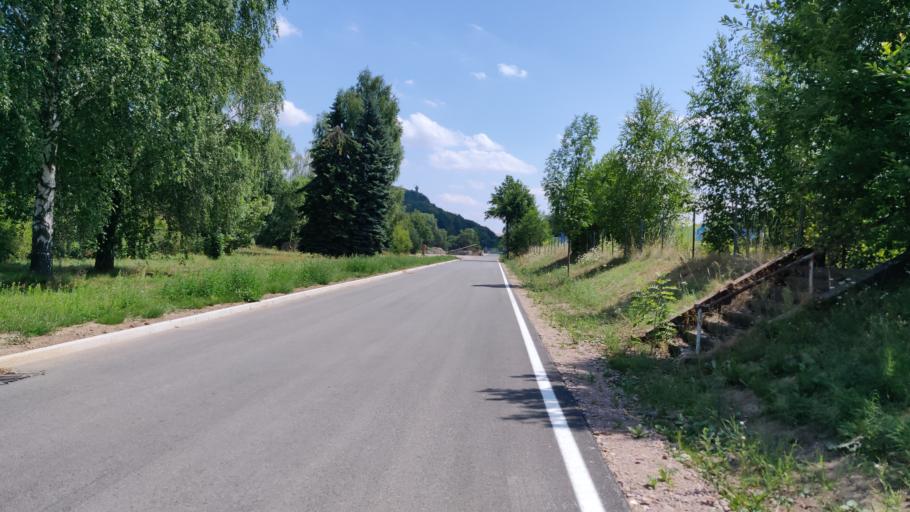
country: DE
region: Saxony
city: Colditz
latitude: 51.1245
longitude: 12.8018
